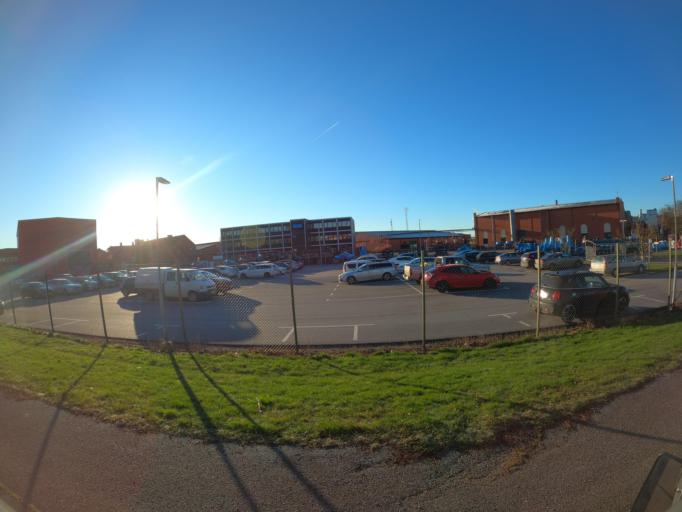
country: SE
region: Skane
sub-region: Svedala Kommun
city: Svedala
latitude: 55.5092
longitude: 13.2298
